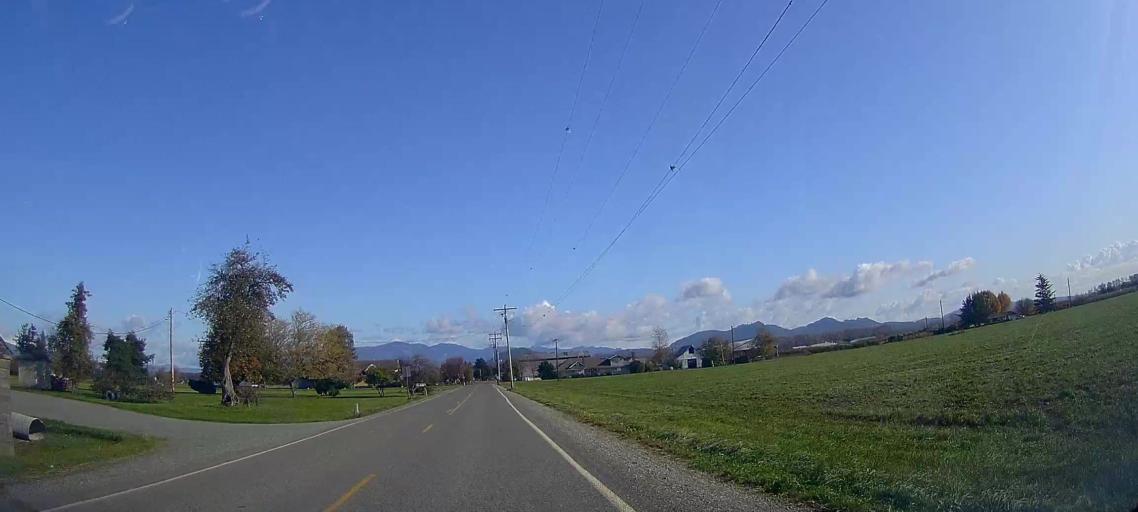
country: US
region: Washington
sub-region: Skagit County
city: Mount Vernon
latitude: 48.3993
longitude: -122.4031
